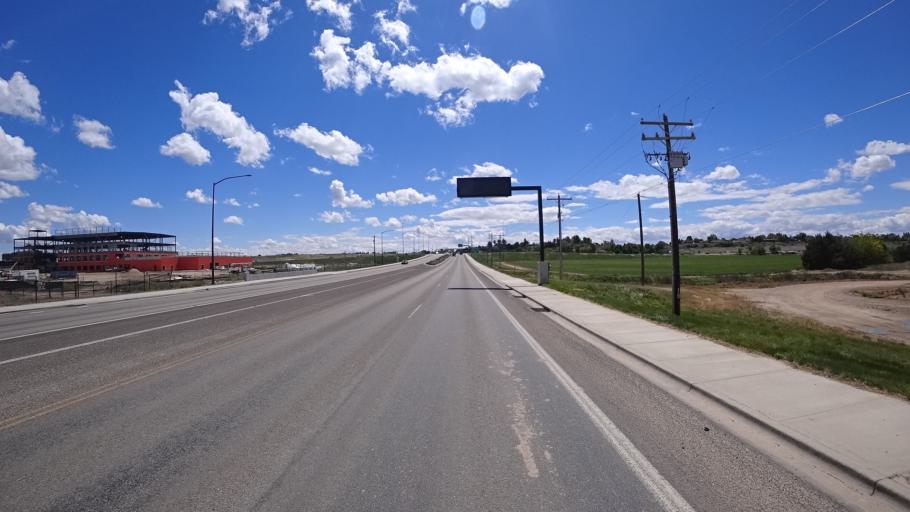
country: US
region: Idaho
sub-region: Ada County
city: Meridian
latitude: 43.5978
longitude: -116.4341
